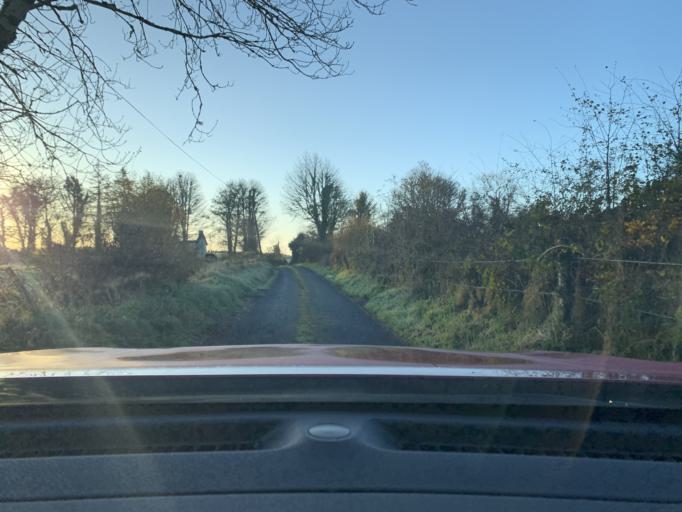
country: IE
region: Connaught
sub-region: Sligo
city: Ballymote
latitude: 54.0615
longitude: -8.5187
